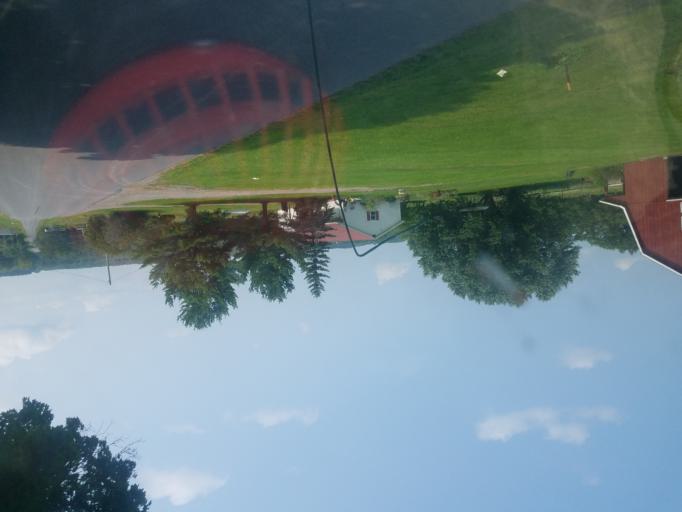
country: US
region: New York
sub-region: Montgomery County
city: Wellsville
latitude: 42.8529
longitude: -74.3508
